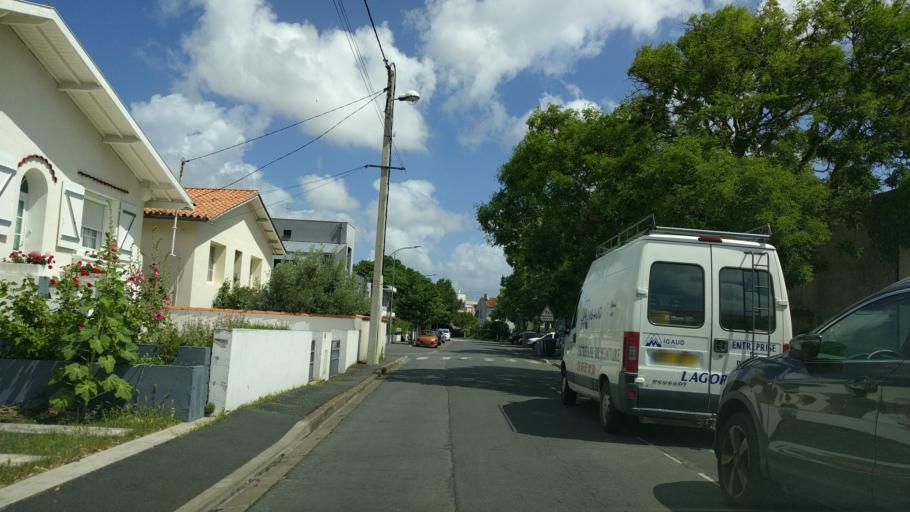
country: FR
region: Poitou-Charentes
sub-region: Departement de la Charente-Maritime
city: La Rochelle
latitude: 46.1732
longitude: -1.1409
